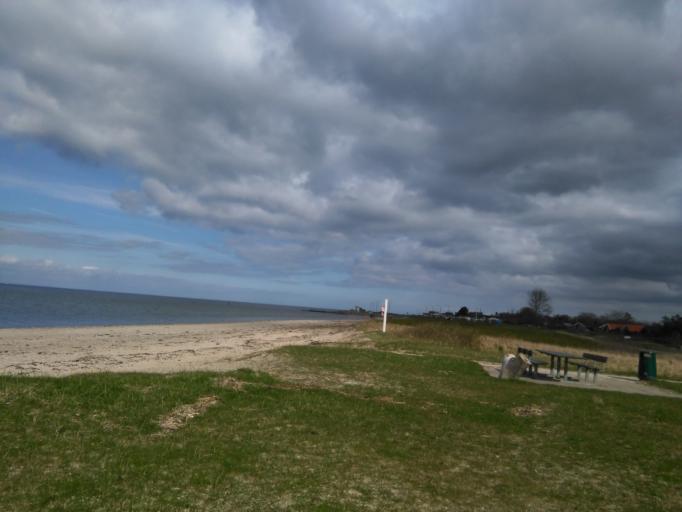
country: DK
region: South Denmark
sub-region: Middelfart Kommune
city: Brenderup
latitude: 55.5148
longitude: 9.9490
